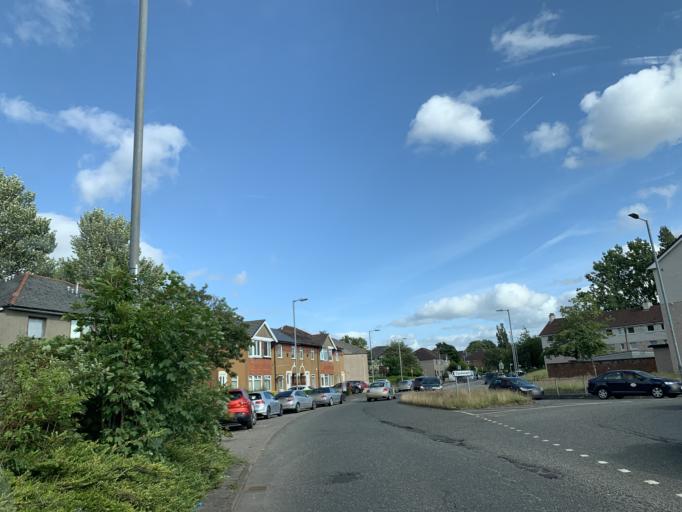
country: GB
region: Scotland
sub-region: Renfrewshire
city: Renfrew
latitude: 55.8516
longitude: -4.3627
